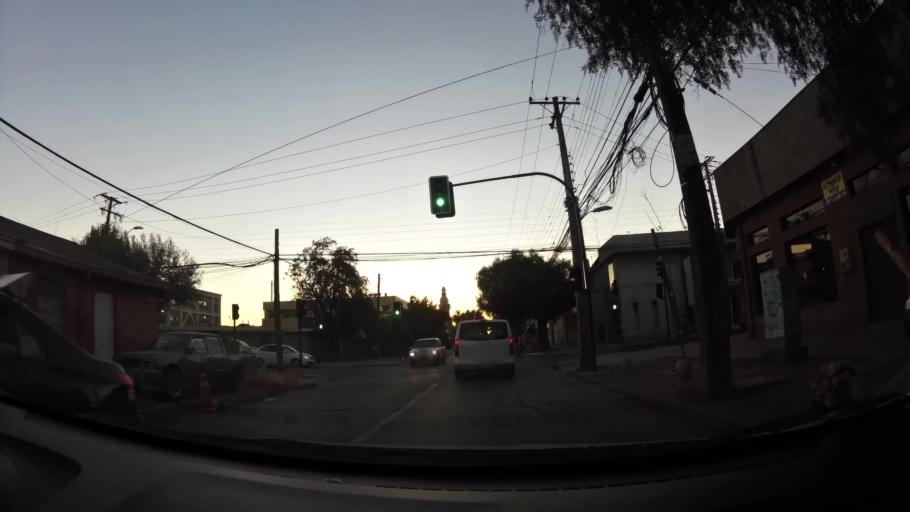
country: CL
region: Maule
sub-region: Provincia de Curico
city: Curico
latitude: -34.9891
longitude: -71.2353
